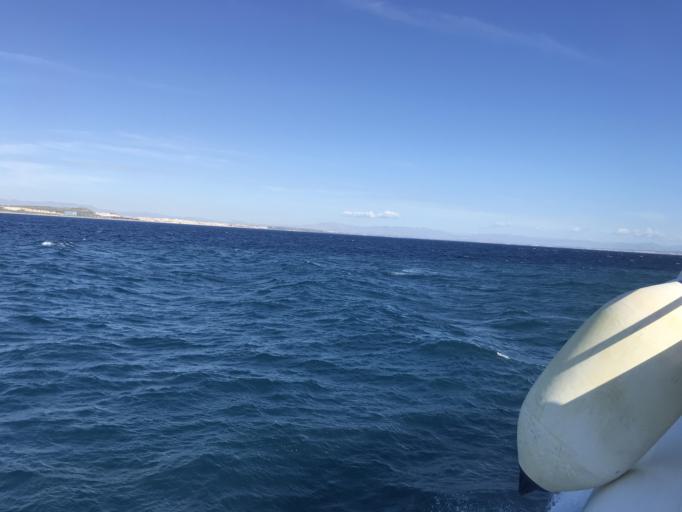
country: ES
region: Valencia
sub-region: Provincia de Alicante
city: Guardamar del Segura
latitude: 38.0275
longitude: -0.6169
